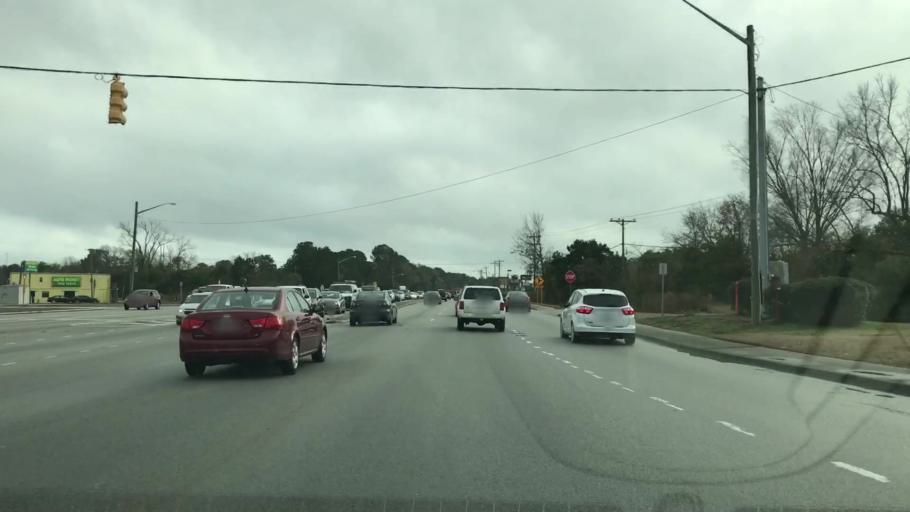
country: US
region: South Carolina
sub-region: Berkeley County
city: Goose Creek
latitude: 32.9962
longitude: -80.0367
